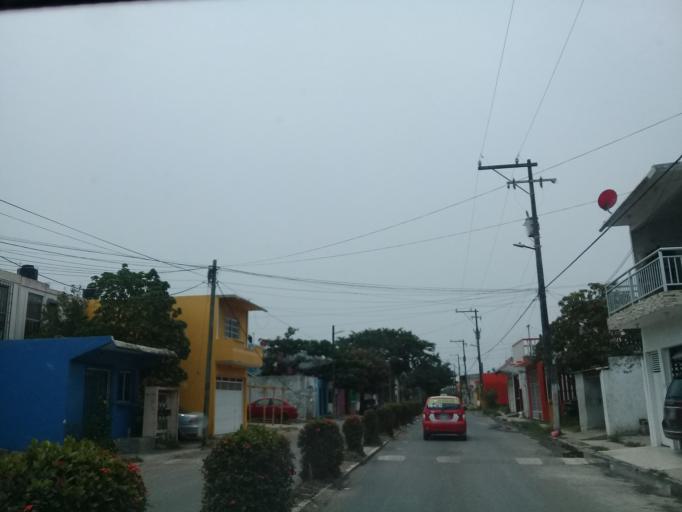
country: MX
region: Veracruz
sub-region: Veracruz
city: Las Amapolas
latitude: 19.1558
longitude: -96.2058
